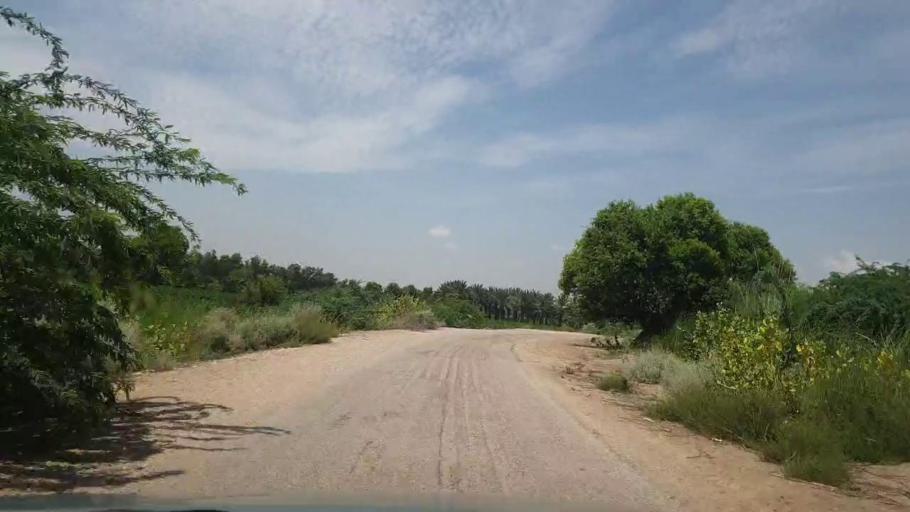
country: PK
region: Sindh
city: Bozdar
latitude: 27.0827
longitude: 68.9798
